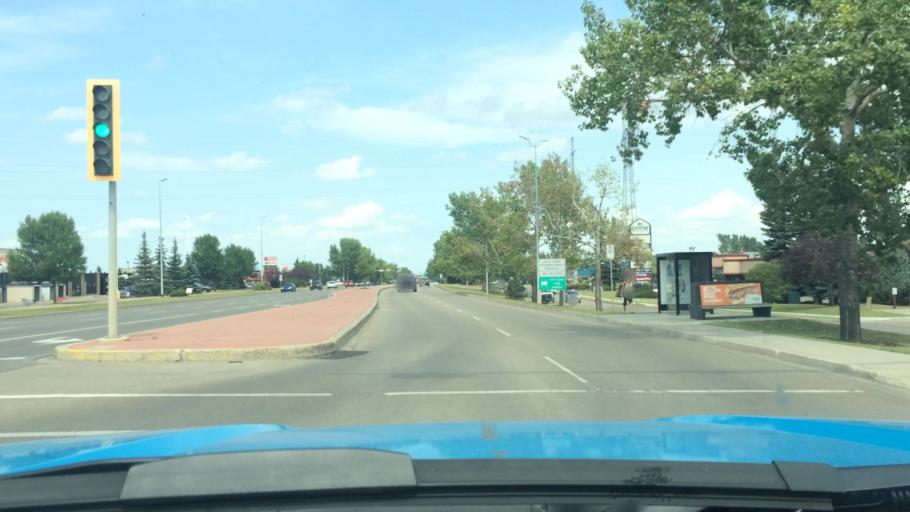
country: CA
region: Alberta
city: Red Deer
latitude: 52.2355
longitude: -113.8139
